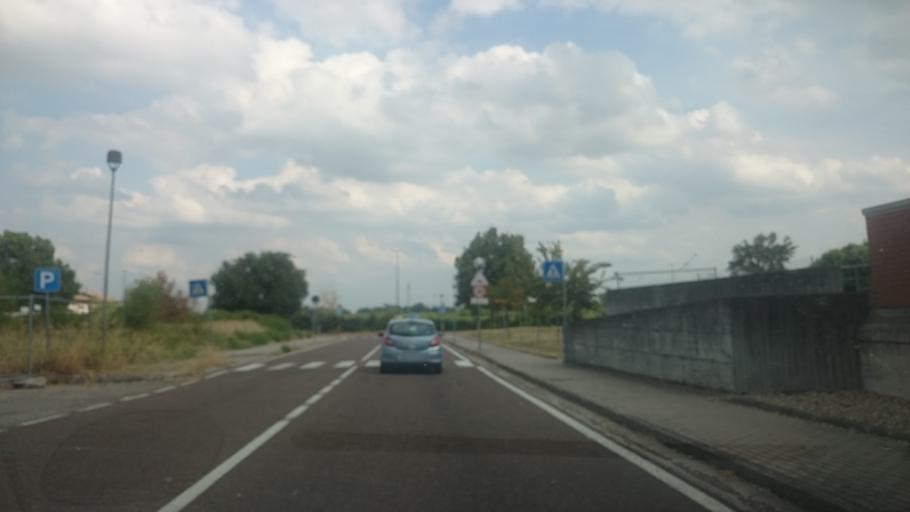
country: IT
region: Emilia-Romagna
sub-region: Provincia di Reggio Emilia
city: Casalgrande
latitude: 44.5879
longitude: 10.7456
